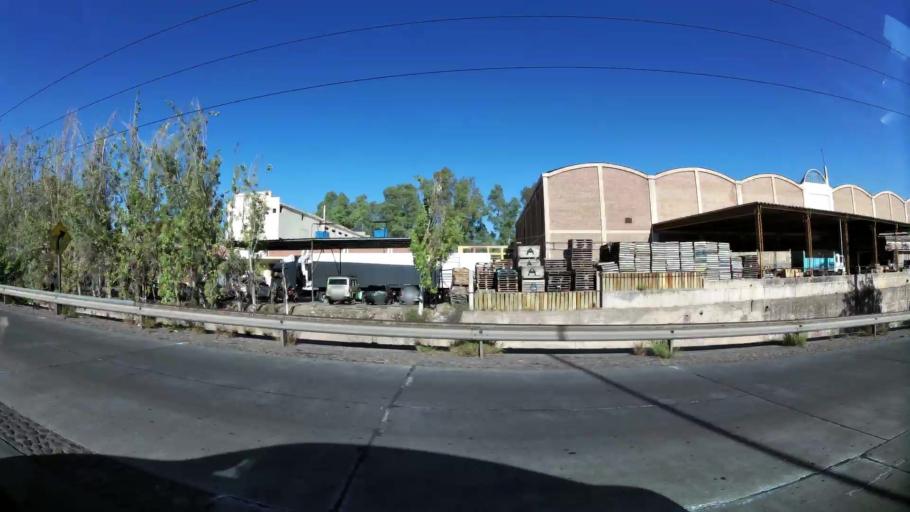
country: AR
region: Mendoza
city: Mendoza
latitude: -32.9074
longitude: -68.8379
